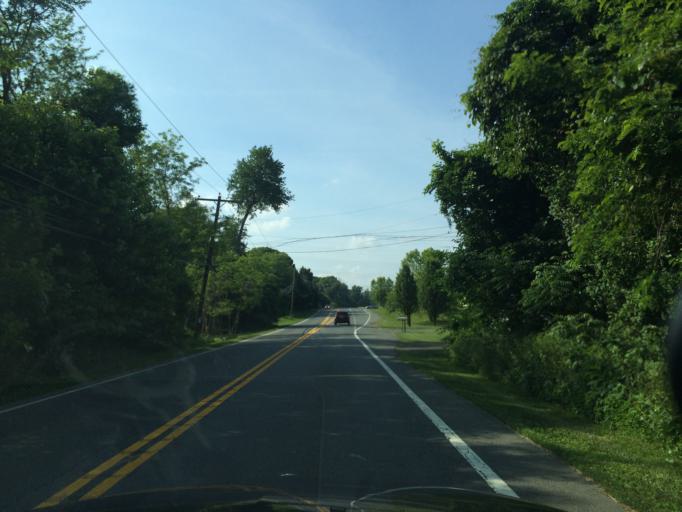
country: US
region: Maryland
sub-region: Montgomery County
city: Olney
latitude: 39.1883
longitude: -77.0649
